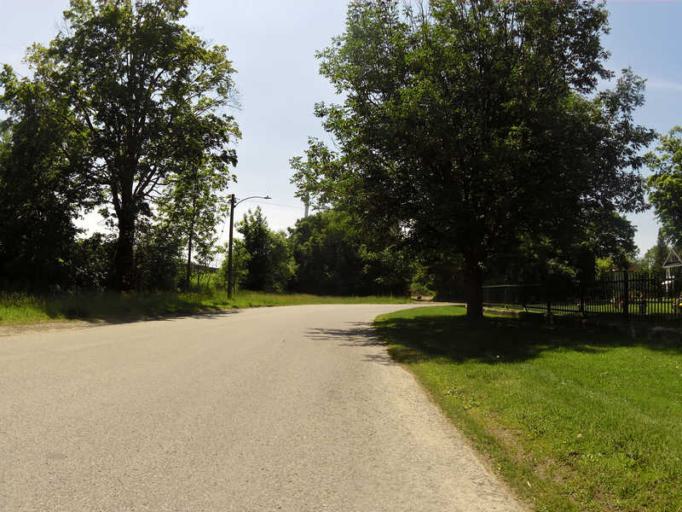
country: CA
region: Ontario
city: Peterborough
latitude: 44.2917
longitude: -78.3093
